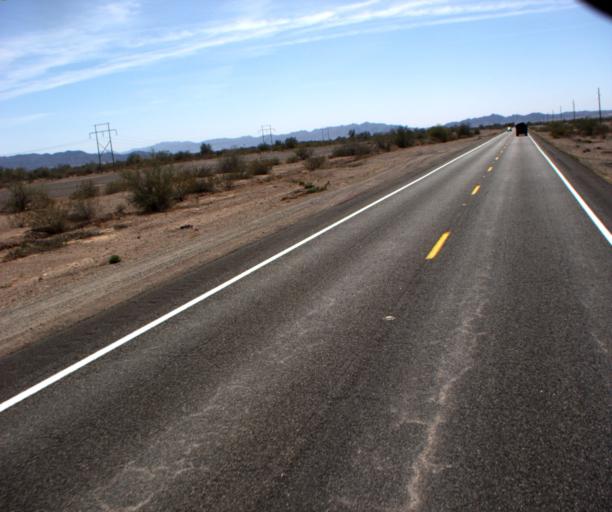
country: US
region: Arizona
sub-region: Yuma County
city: Fortuna Foothills
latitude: 32.9026
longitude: -114.3320
